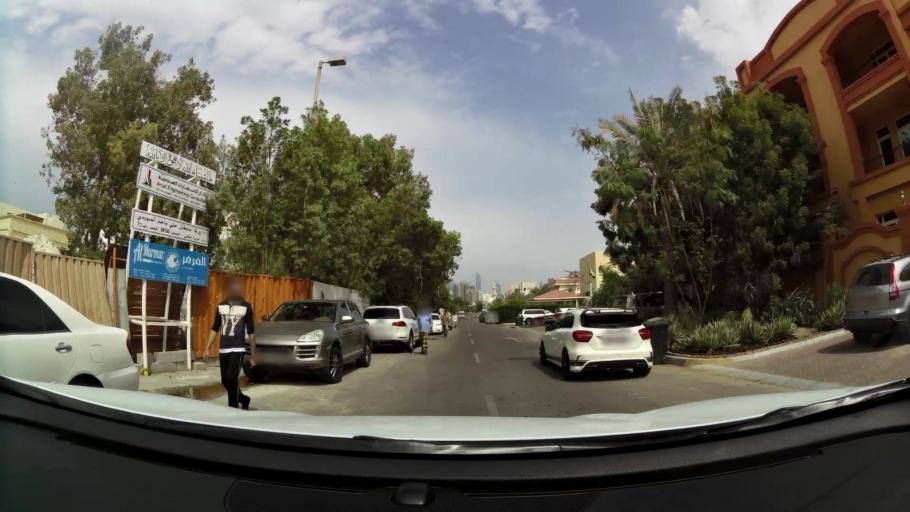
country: AE
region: Abu Dhabi
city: Abu Dhabi
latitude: 24.4596
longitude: 54.3349
